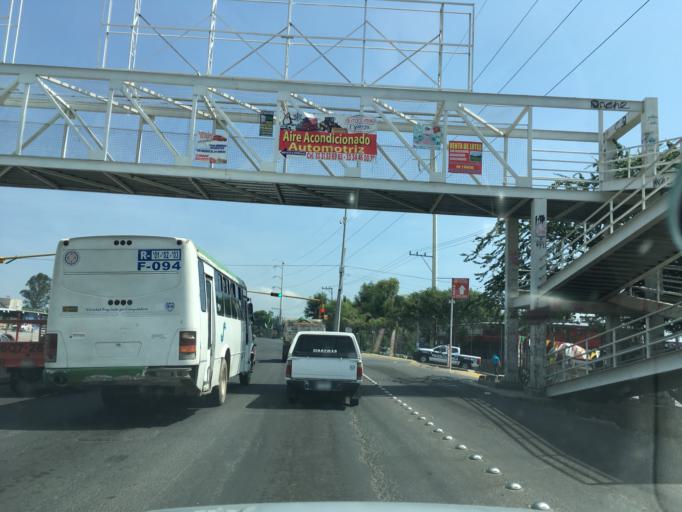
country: MX
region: Jalisco
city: Tonala
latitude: 20.6612
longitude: -103.2320
